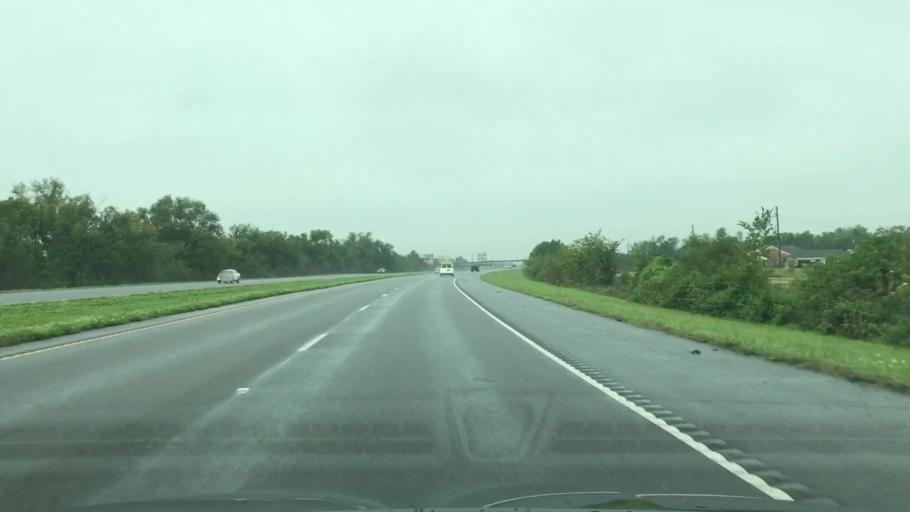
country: US
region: Louisiana
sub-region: Lafourche Parish
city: Raceland
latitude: 29.6907
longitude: -90.5934
